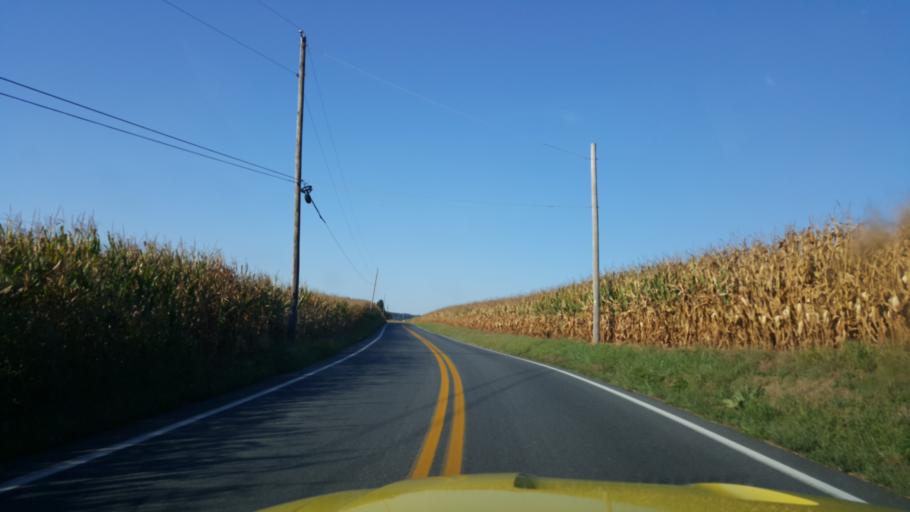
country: US
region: Pennsylvania
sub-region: Lancaster County
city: Rheems
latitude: 40.1895
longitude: -76.5176
